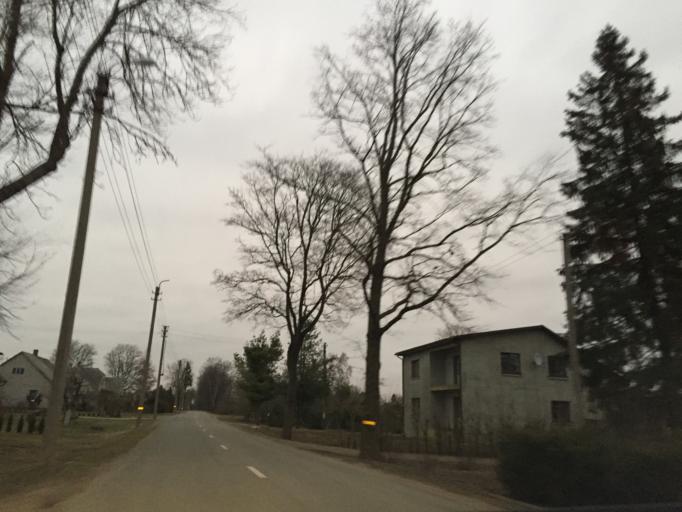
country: LT
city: Zagare
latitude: 56.3390
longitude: 23.2973
